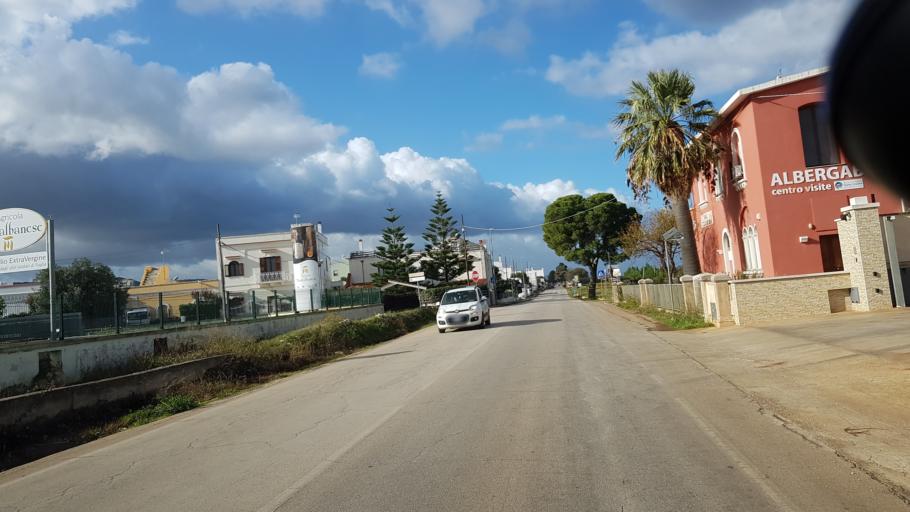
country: IT
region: Apulia
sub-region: Provincia di Brindisi
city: Montalbano
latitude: 40.7806
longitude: 17.4844
